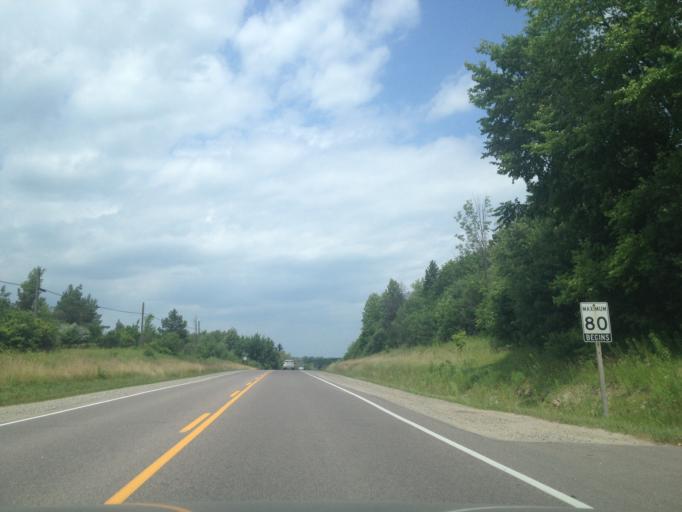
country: CA
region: Ontario
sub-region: Wellington County
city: Guelph
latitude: 43.5808
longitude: -80.2460
